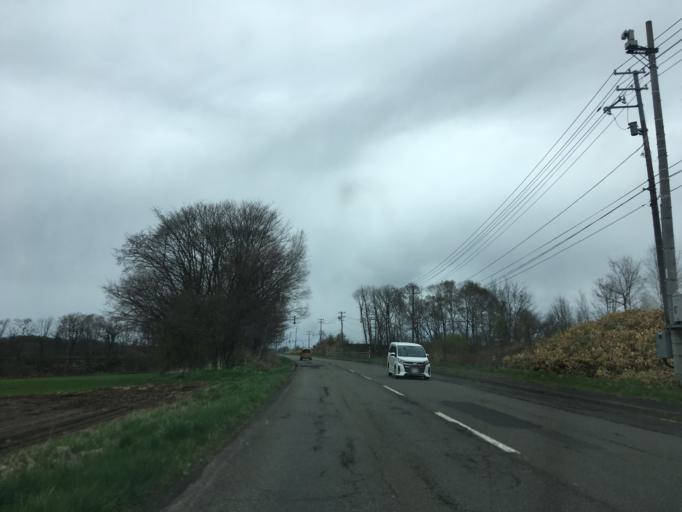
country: JP
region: Hokkaido
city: Chitose
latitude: 42.8988
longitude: 141.8138
